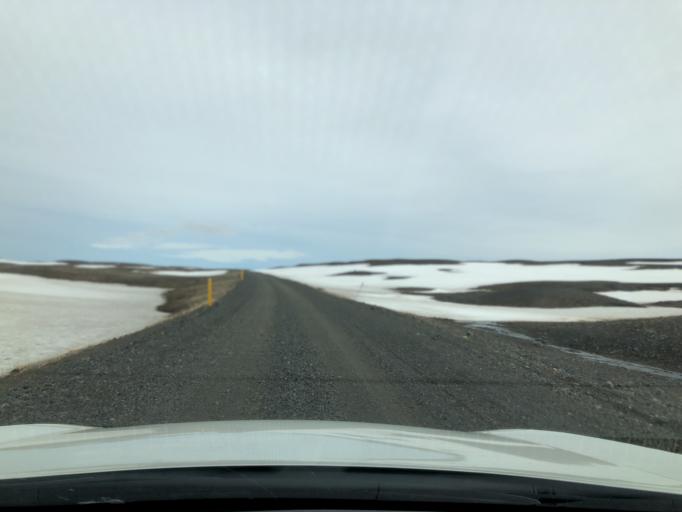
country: IS
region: East
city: Egilsstadir
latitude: 65.3036
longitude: -15.3995
